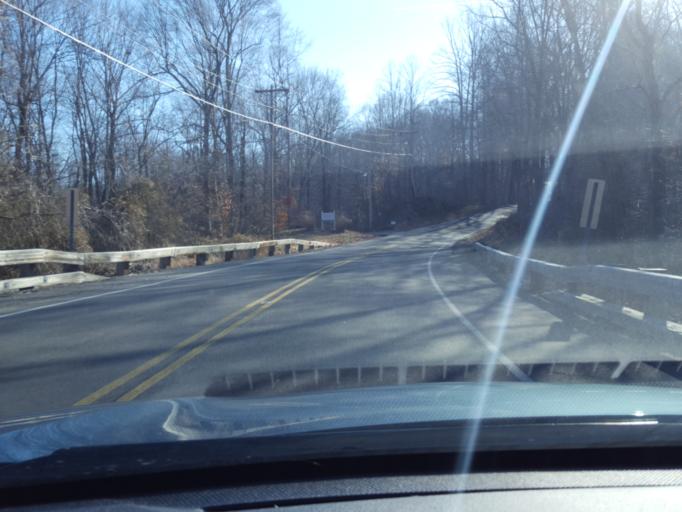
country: US
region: Maryland
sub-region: Calvert County
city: Chesapeake Beach
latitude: 38.6516
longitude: -76.5703
